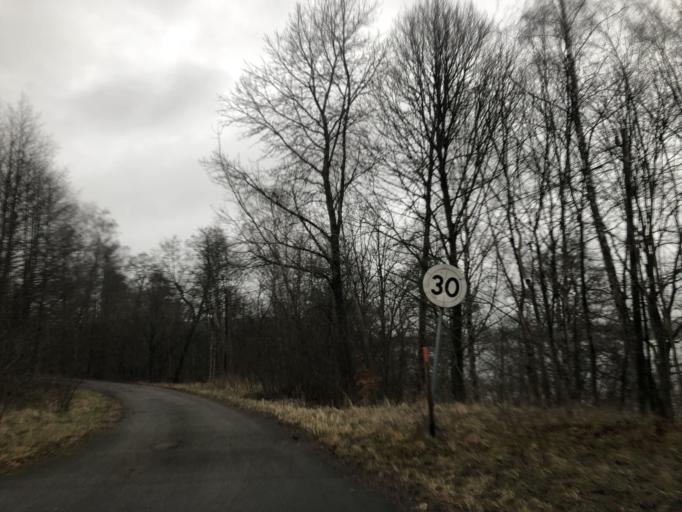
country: SE
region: Vaestra Goetaland
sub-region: Ulricehamns Kommun
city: Ulricehamn
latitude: 57.7902
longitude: 13.3922
